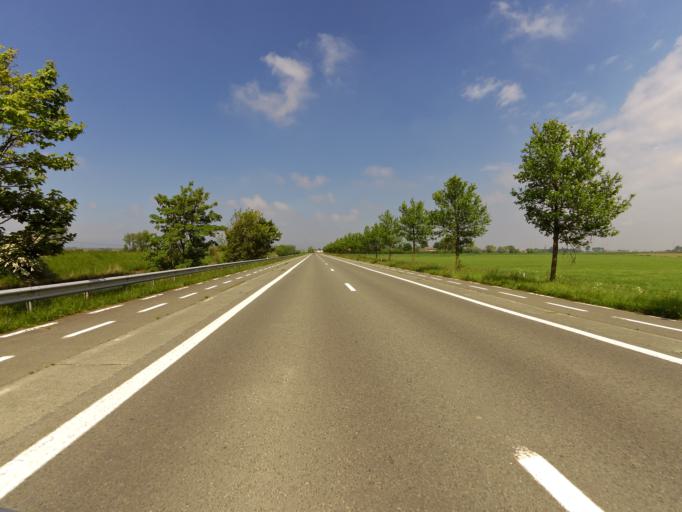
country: BE
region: Flanders
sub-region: Provincie West-Vlaanderen
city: Veurne
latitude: 51.0903
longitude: 2.6759
